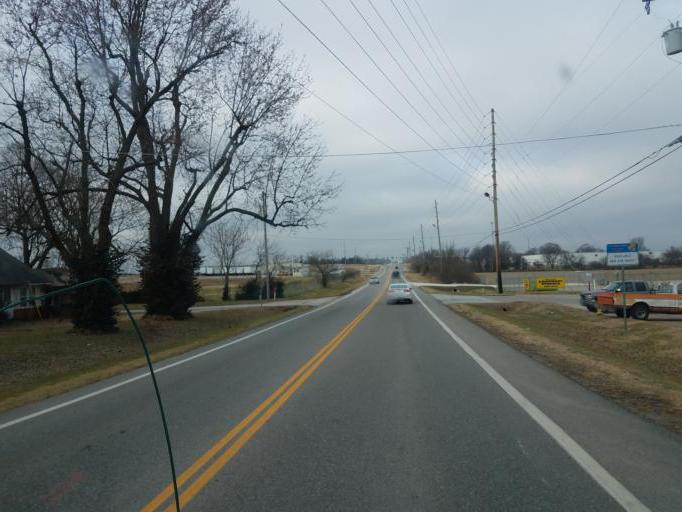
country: US
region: Missouri
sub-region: Greene County
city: Springfield
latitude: 37.2385
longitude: -93.2104
